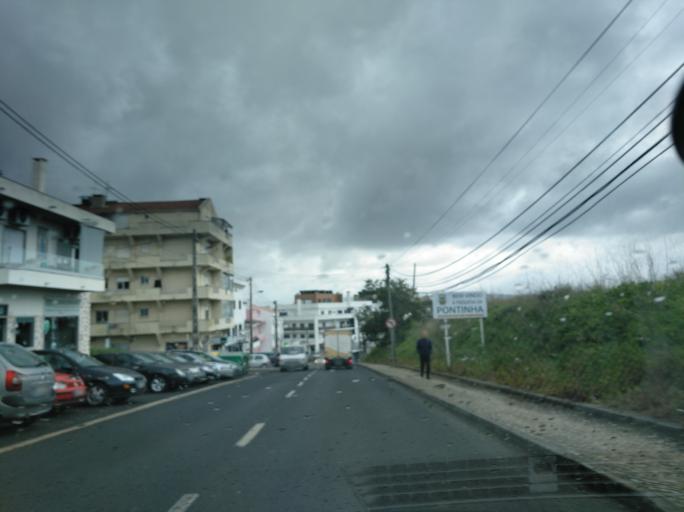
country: PT
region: Lisbon
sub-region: Odivelas
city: Famoes
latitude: 38.7849
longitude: -9.2077
